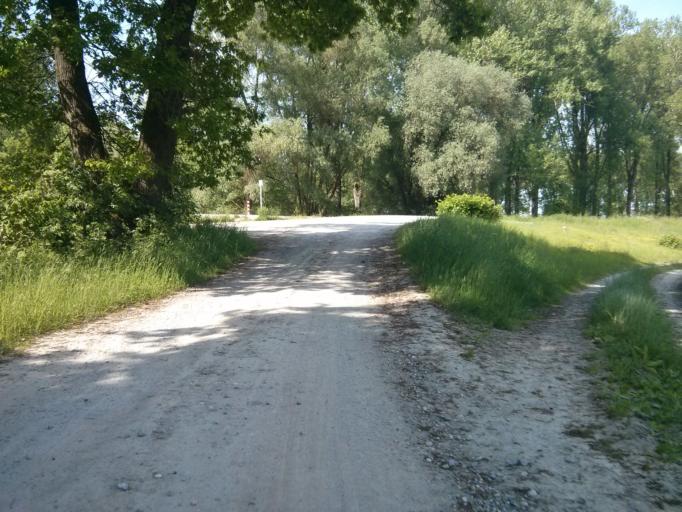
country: DE
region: Bavaria
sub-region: Lower Bavaria
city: Plattling
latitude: 48.7761
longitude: 12.8985
